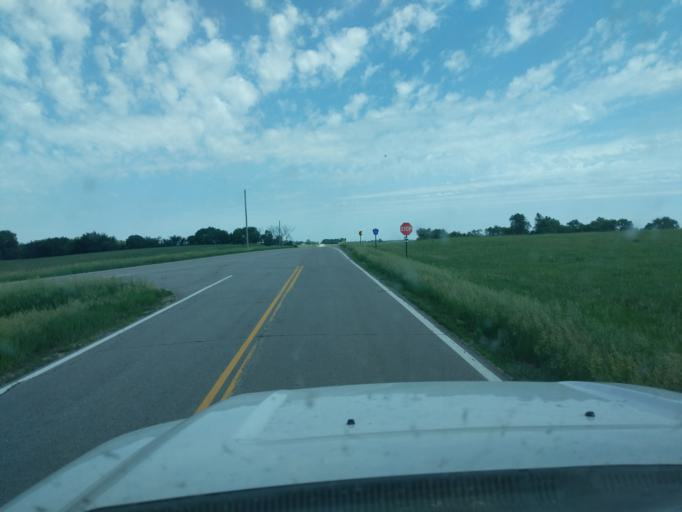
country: US
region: Minnesota
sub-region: Yellow Medicine County
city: Granite Falls
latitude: 44.7466
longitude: -95.4019
